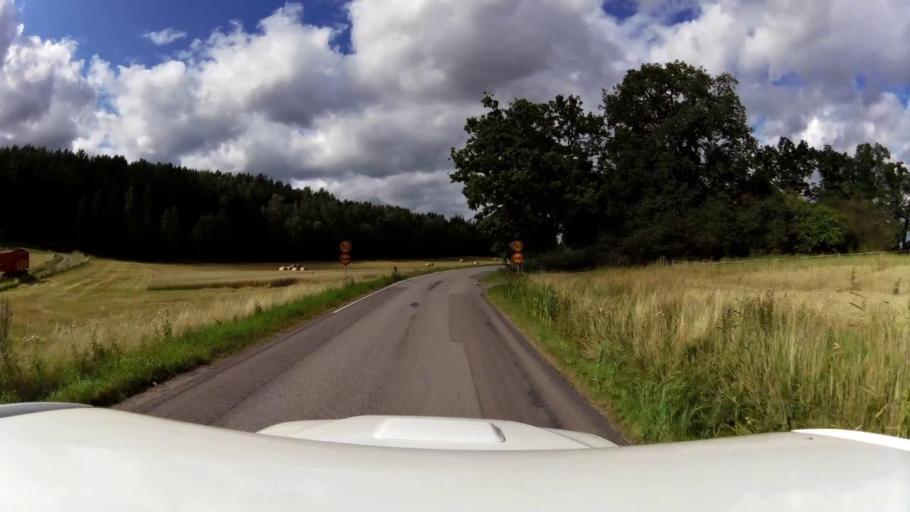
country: SE
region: OEstergoetland
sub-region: Linkopings Kommun
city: Sturefors
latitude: 58.3208
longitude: 15.7191
